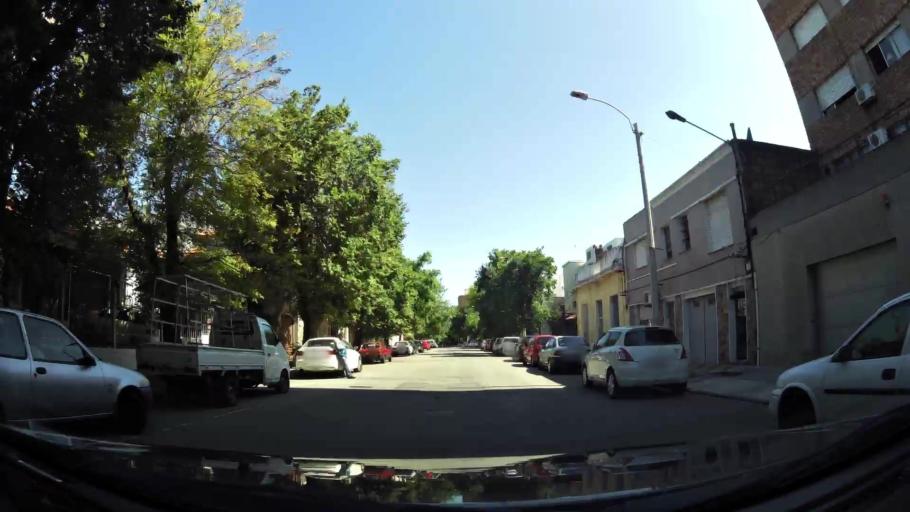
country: UY
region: Montevideo
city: Montevideo
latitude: -34.9037
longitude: -56.1605
